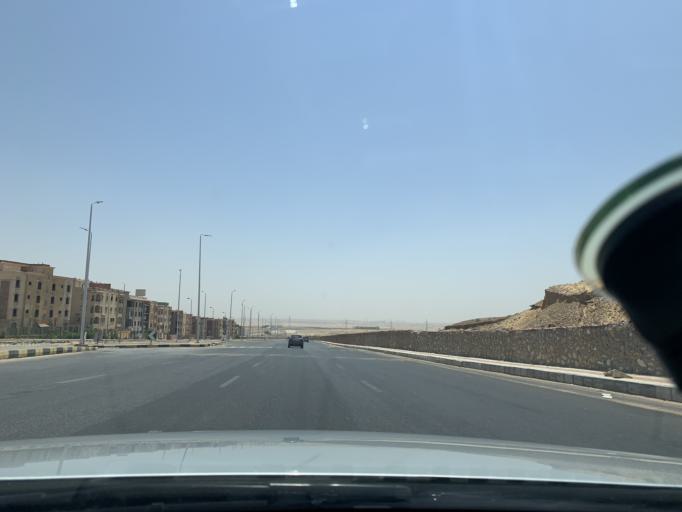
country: EG
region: Muhafazat al Qahirah
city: Halwan
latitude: 29.9848
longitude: 31.4686
